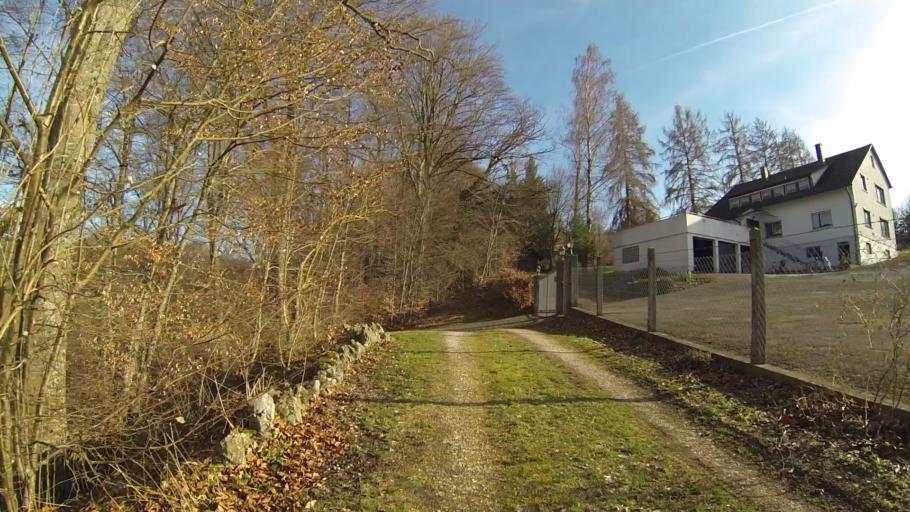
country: DE
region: Baden-Wuerttemberg
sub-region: Regierungsbezirk Stuttgart
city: Hermaringen
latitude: 48.5812
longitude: 10.2242
